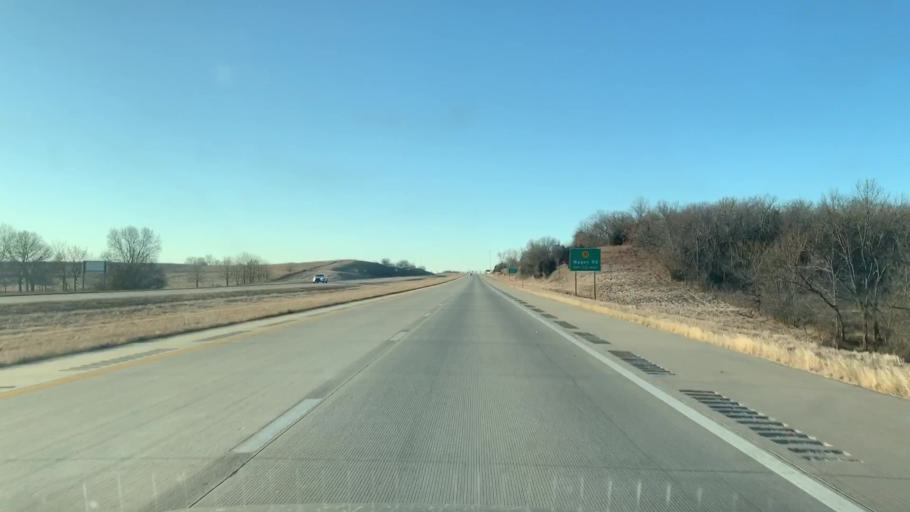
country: US
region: Kansas
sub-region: Bourbon County
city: Fort Scott
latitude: 38.0060
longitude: -94.7044
